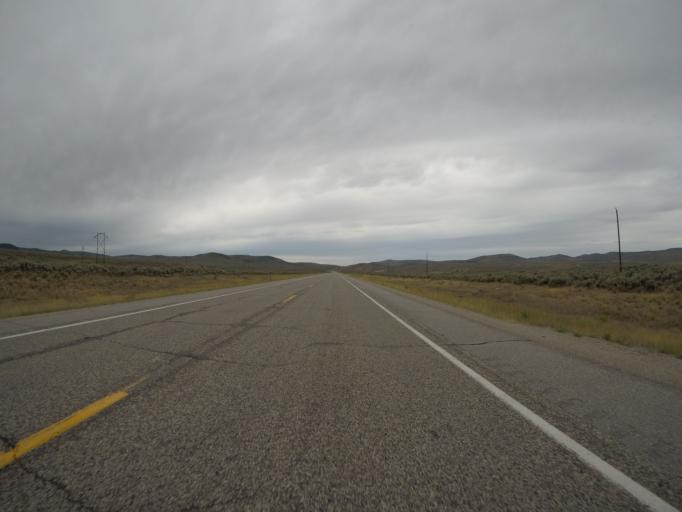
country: US
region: Wyoming
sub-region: Lincoln County
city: Kemmerer
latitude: 41.8154
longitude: -110.7557
